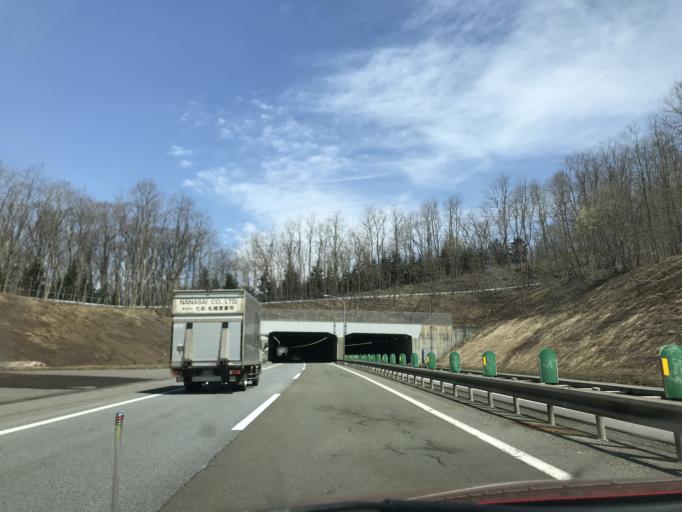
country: JP
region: Hokkaido
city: Bibai
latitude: 43.2873
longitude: 141.8620
